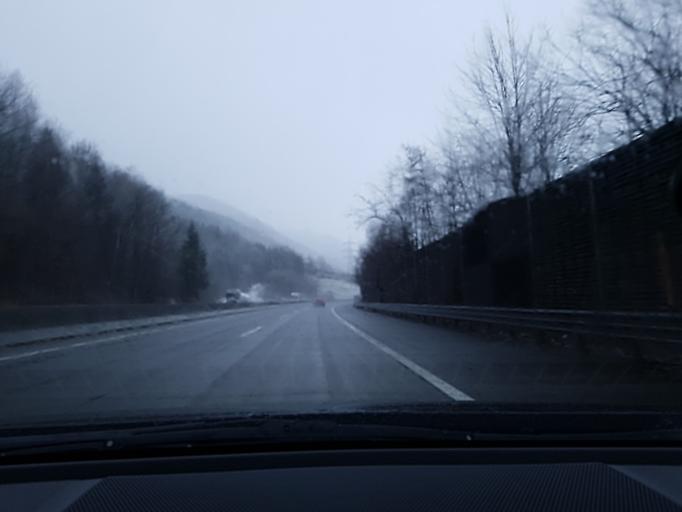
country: AT
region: Salzburg
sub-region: Politischer Bezirk Hallein
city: Kuchl
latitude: 47.6261
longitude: 13.1340
